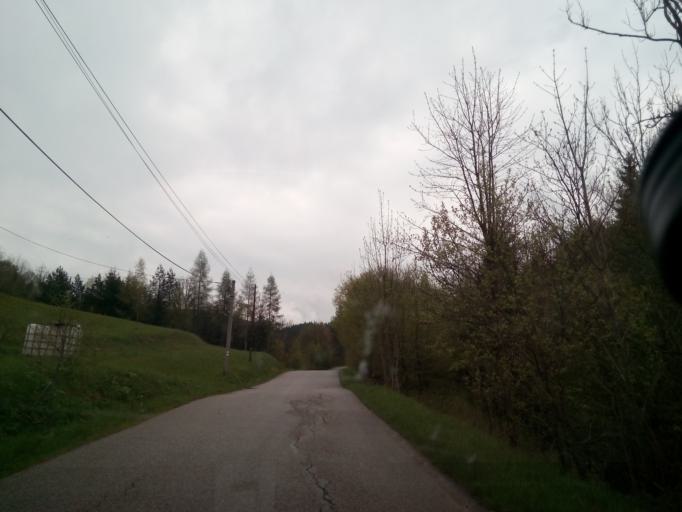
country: SK
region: Zilinsky
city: Oravska Lesna
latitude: 49.2982
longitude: 19.1884
